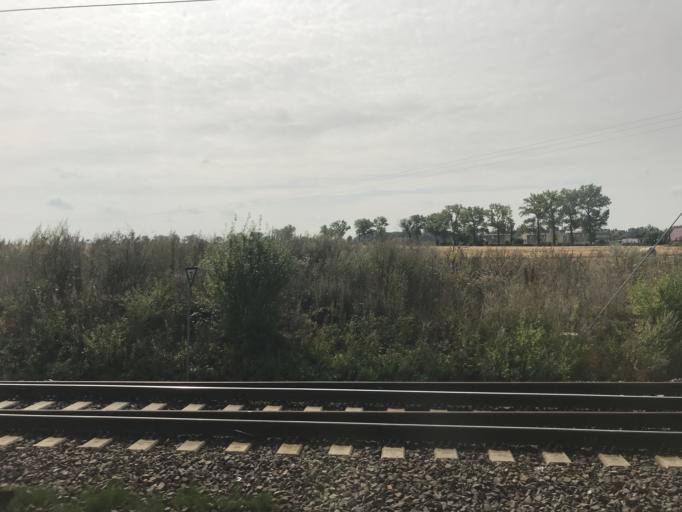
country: PL
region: Kujawsko-Pomorskie
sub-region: Powiat inowroclawski
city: Janikowo
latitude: 52.7817
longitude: 18.1816
